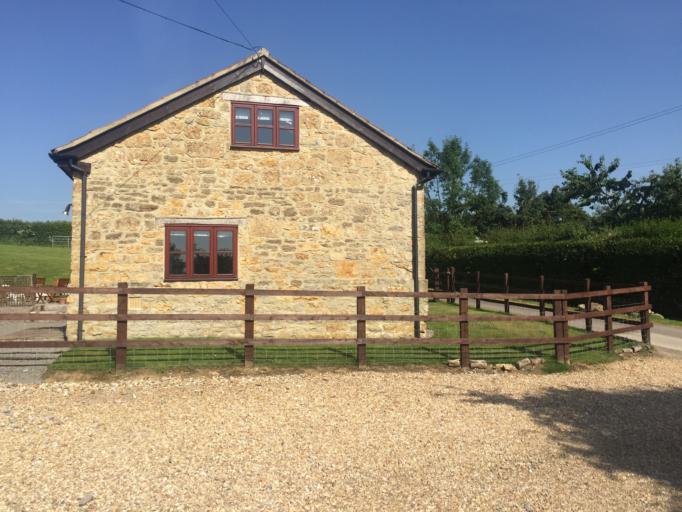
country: GB
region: England
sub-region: Dorset
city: Bridport
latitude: 50.7640
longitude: -2.7406
